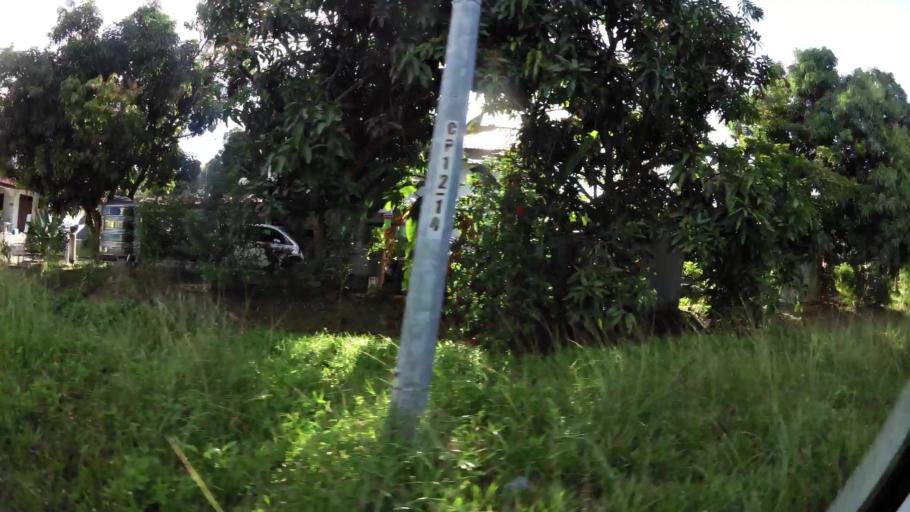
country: BN
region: Brunei and Muara
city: Bandar Seri Begawan
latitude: 4.9845
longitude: 114.9641
